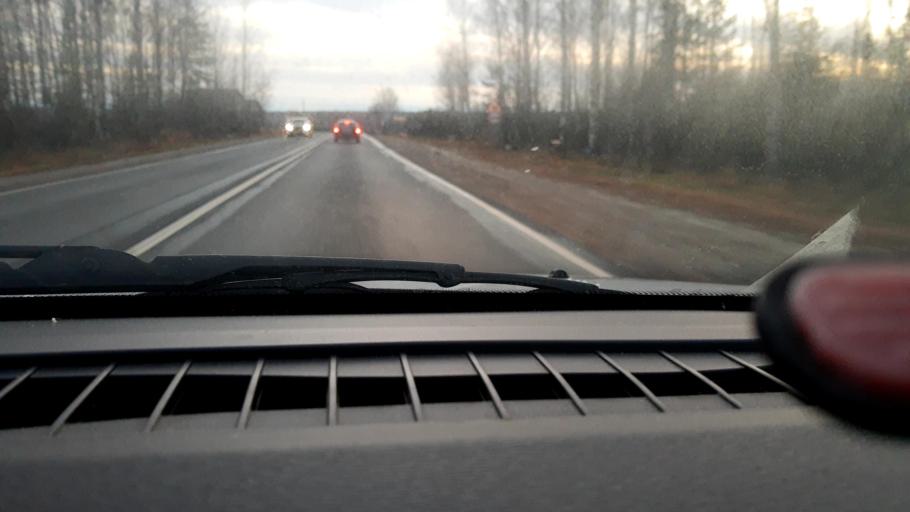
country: RU
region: Nizjnij Novgorod
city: Krasnyye Baki
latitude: 57.0713
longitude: 45.1402
